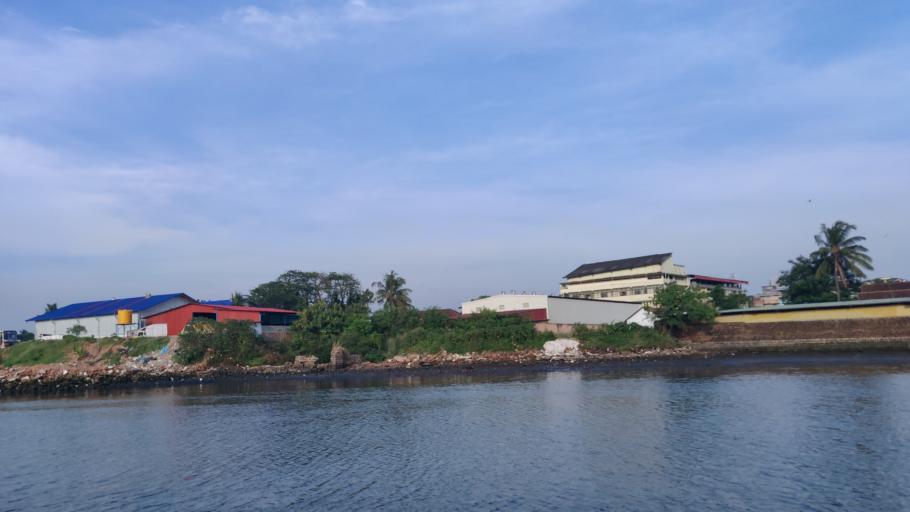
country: IN
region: Karnataka
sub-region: Dakshina Kannada
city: Mangalore
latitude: 12.8675
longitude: 74.8300
